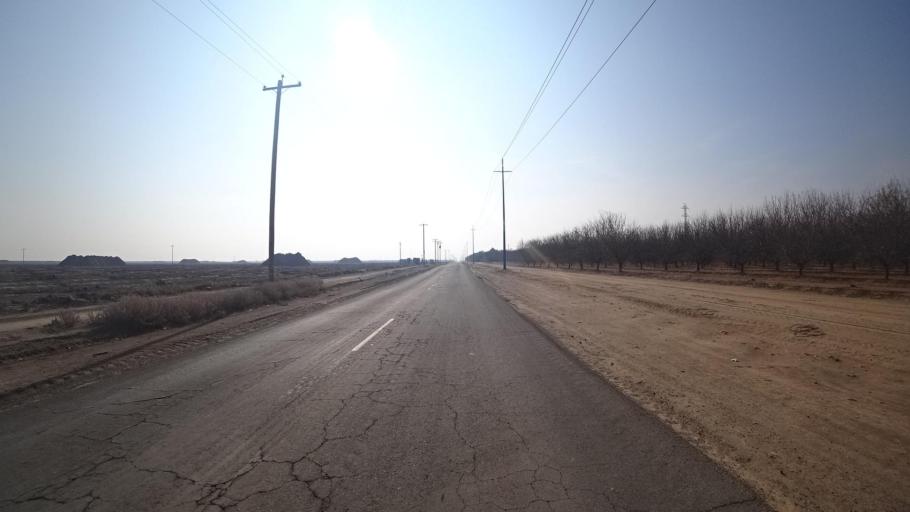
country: US
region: California
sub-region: Kern County
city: Buttonwillow
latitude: 35.4258
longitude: -119.4472
